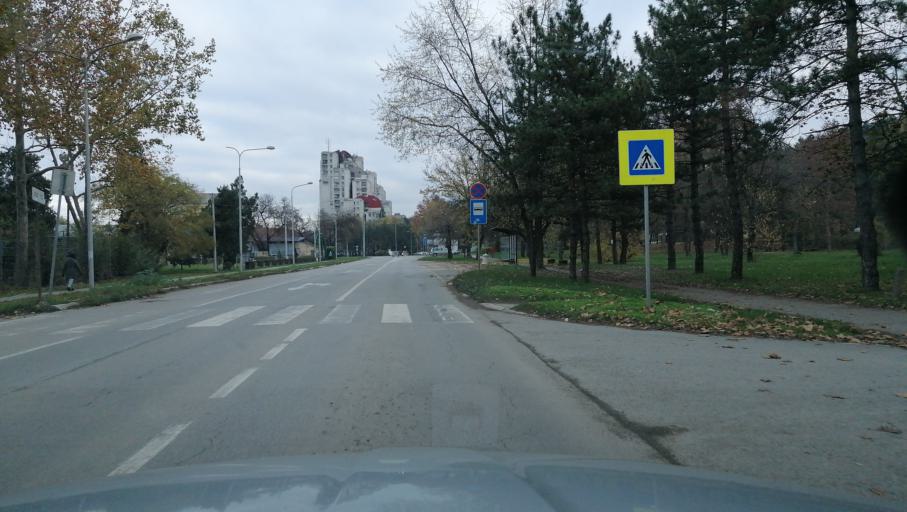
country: RS
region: Central Serbia
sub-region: Podunavski Okrug
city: Smederevo
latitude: 44.6643
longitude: 20.9133
